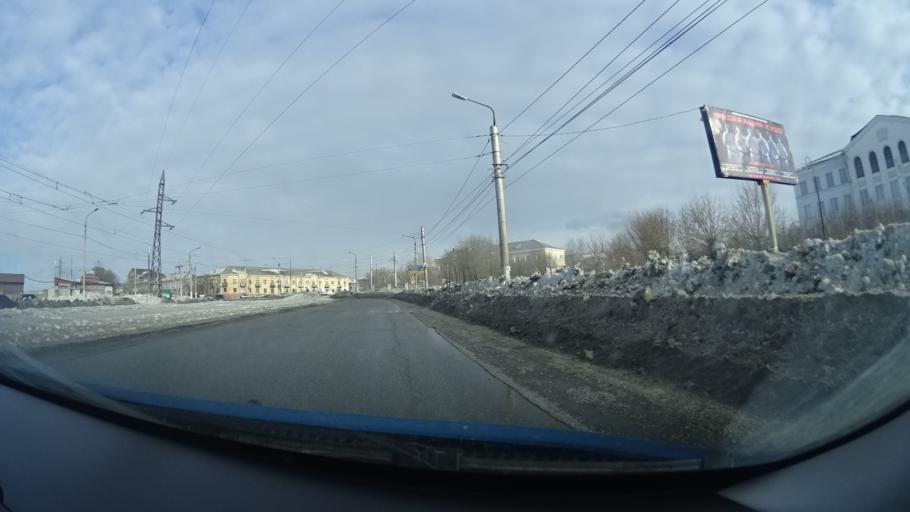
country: RU
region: Chelyabinsk
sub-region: Gorod Magnitogorsk
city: Magnitogorsk
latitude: 53.4344
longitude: 58.9889
